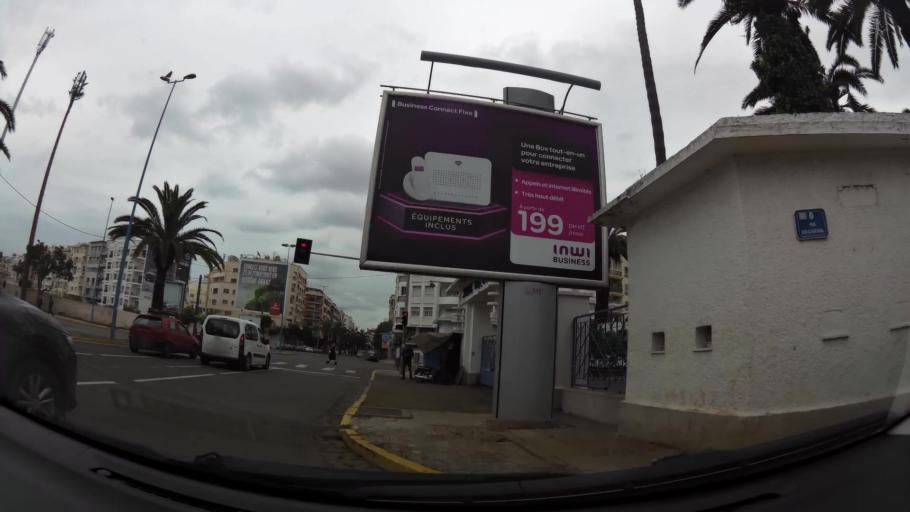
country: MA
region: Grand Casablanca
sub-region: Casablanca
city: Casablanca
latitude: 33.5903
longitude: -7.6460
